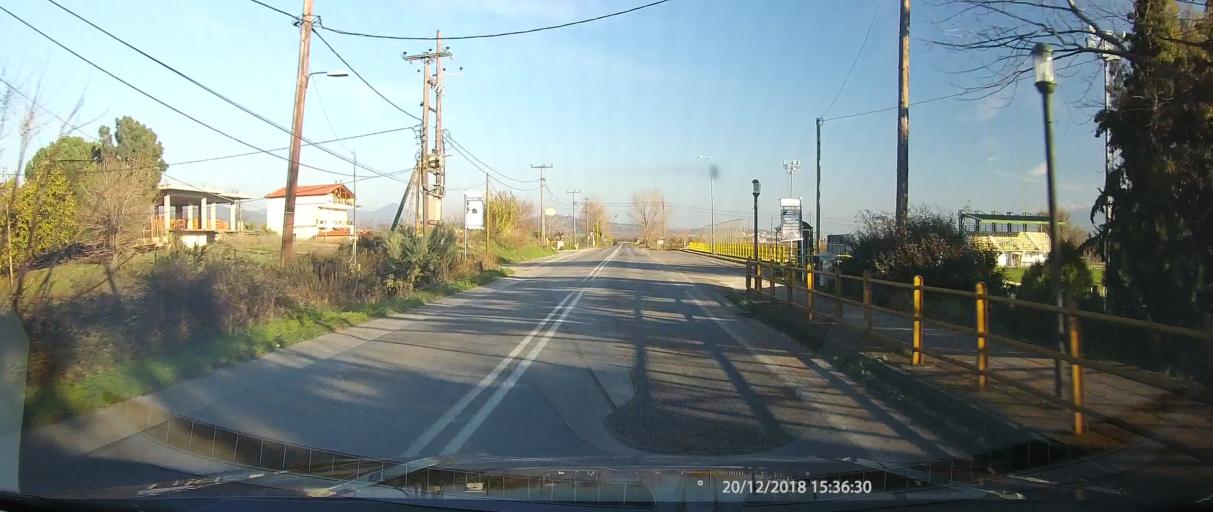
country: GR
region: Central Greece
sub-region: Nomos Fthiotidos
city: Lianokladhion
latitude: 38.9156
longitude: 22.3111
